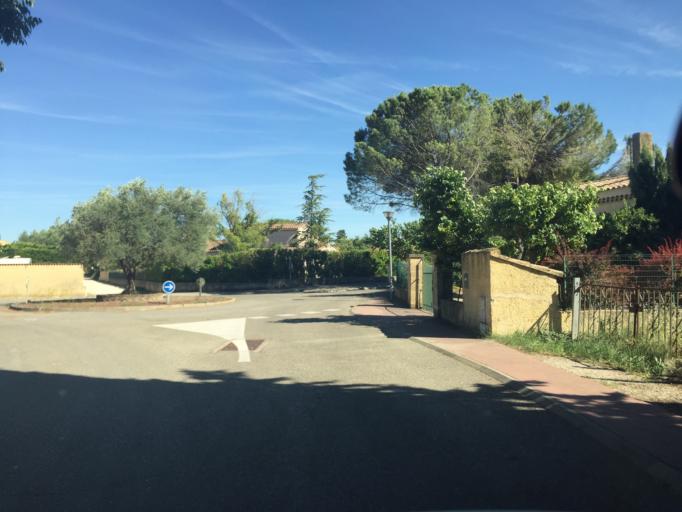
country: FR
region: Provence-Alpes-Cote d'Azur
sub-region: Departement du Vaucluse
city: Caderousse
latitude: 44.1063
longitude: 4.7593
